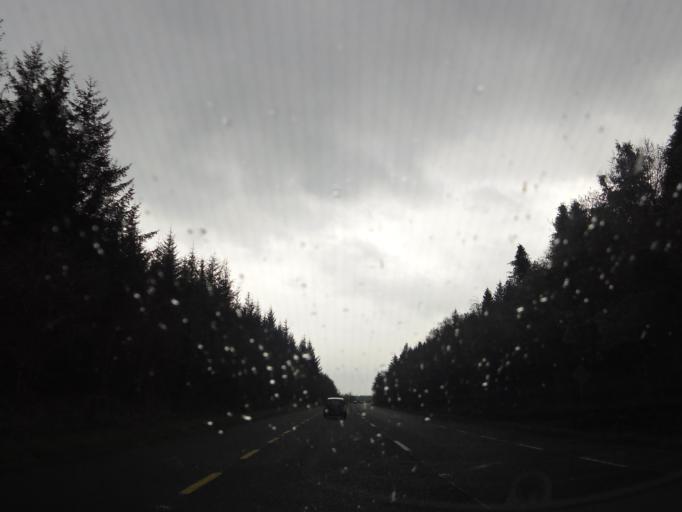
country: IE
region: Connaught
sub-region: Maigh Eo
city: Claremorris
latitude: 53.6997
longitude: -8.9781
